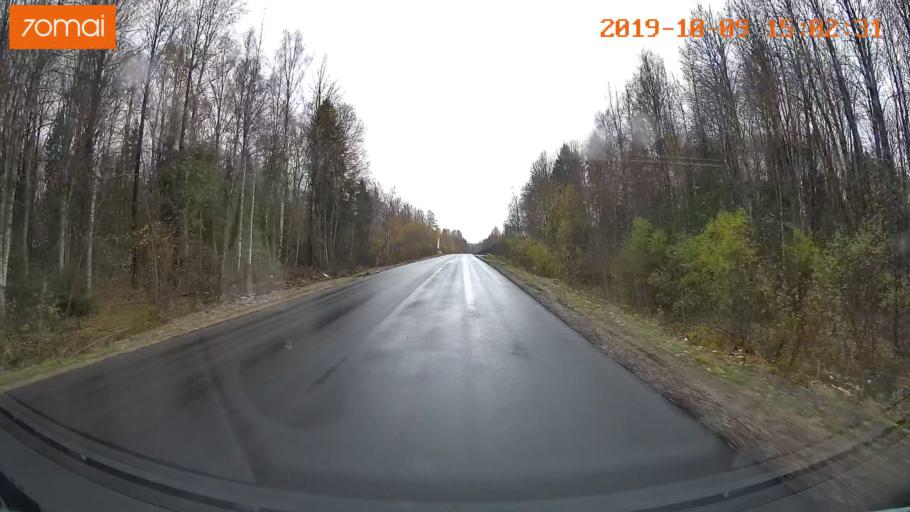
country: RU
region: Kostroma
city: Chistyye Bory
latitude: 58.2839
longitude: 41.6786
